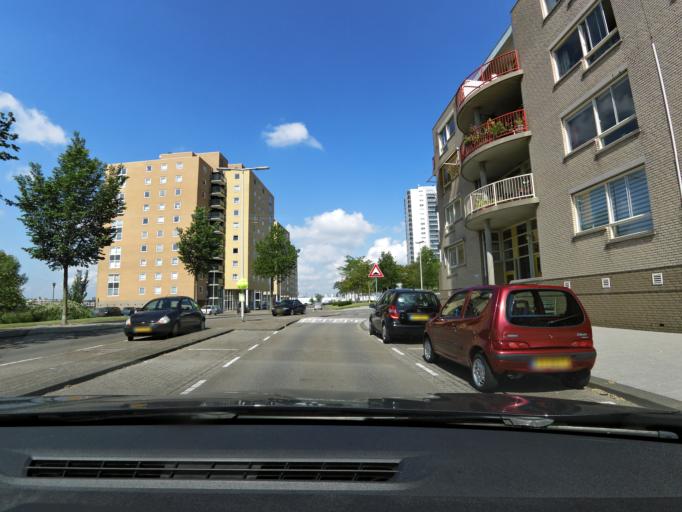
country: NL
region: South Holland
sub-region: Gemeente Rotterdam
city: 's-Gravenland
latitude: 51.9069
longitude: 4.5224
